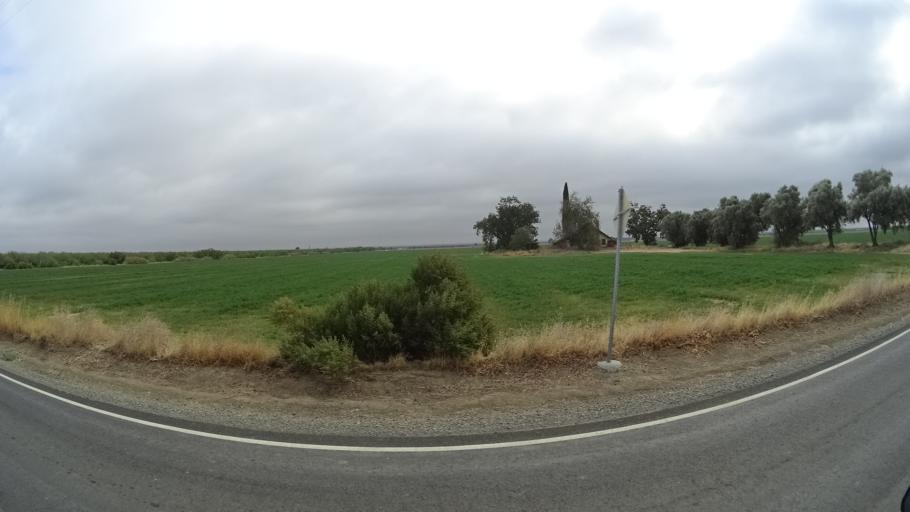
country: US
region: California
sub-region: Yolo County
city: Esparto
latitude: 38.7582
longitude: -122.0444
